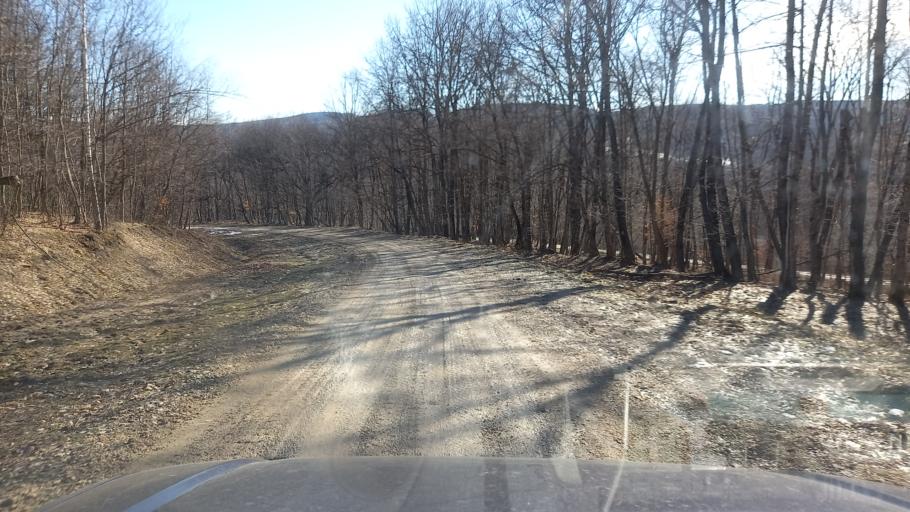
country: RU
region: Adygeya
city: Kamennomostskiy
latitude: 44.2834
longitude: 40.3174
